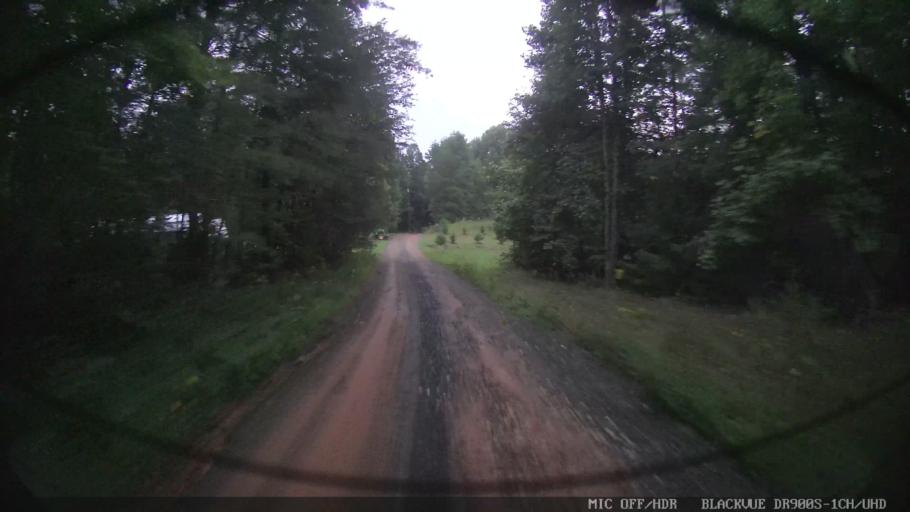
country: US
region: Georgia
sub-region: Gilmer County
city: Ellijay
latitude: 34.6976
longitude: -84.3296
